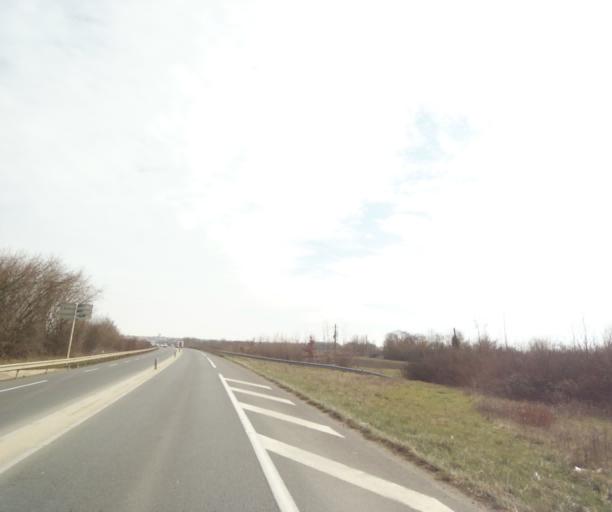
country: FR
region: Poitou-Charentes
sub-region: Departement des Deux-Sevres
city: Niort
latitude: 46.2941
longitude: -0.4520
